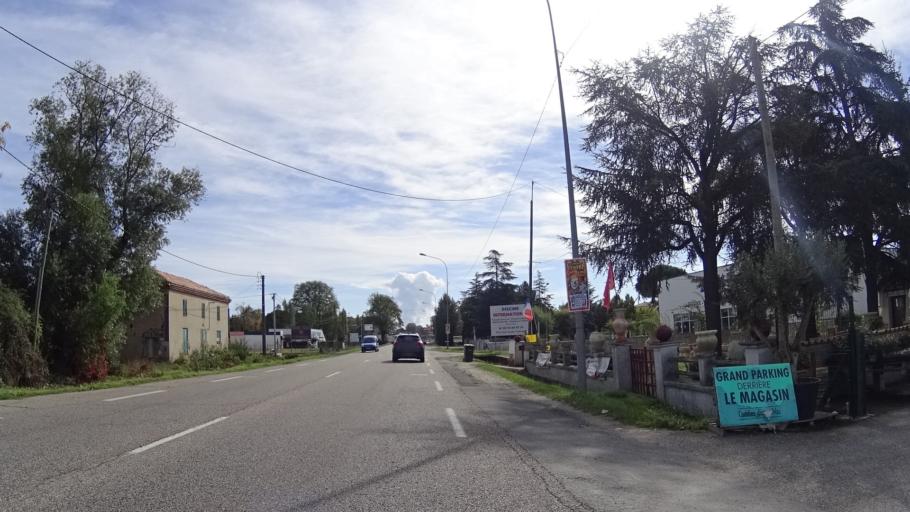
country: FR
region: Aquitaine
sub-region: Departement du Lot-et-Garonne
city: Castelculier
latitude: 44.1715
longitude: 0.6944
